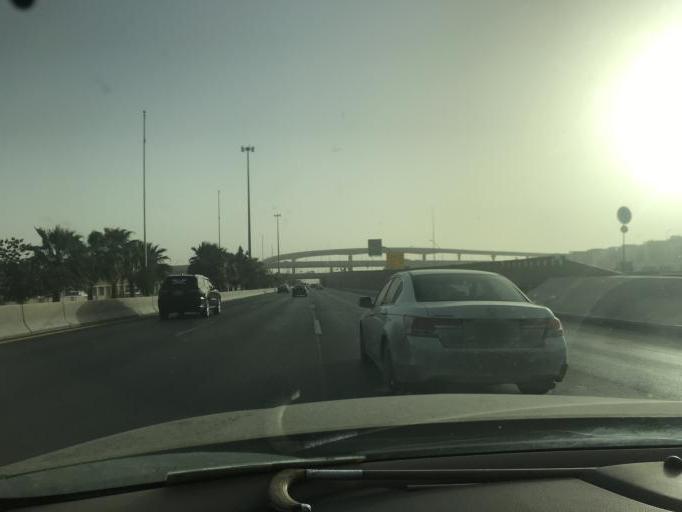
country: SA
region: Ar Riyad
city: Riyadh
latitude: 24.8413
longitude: 46.6496
